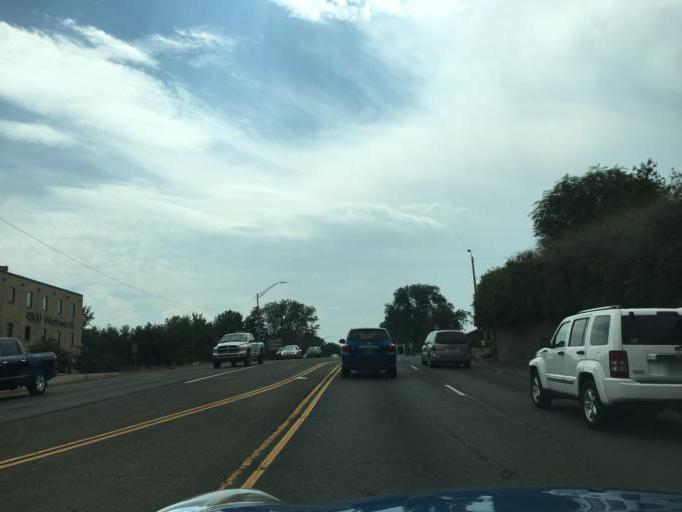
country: US
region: Colorado
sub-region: Jefferson County
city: Wheat Ridge
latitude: 39.7831
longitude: -105.0815
